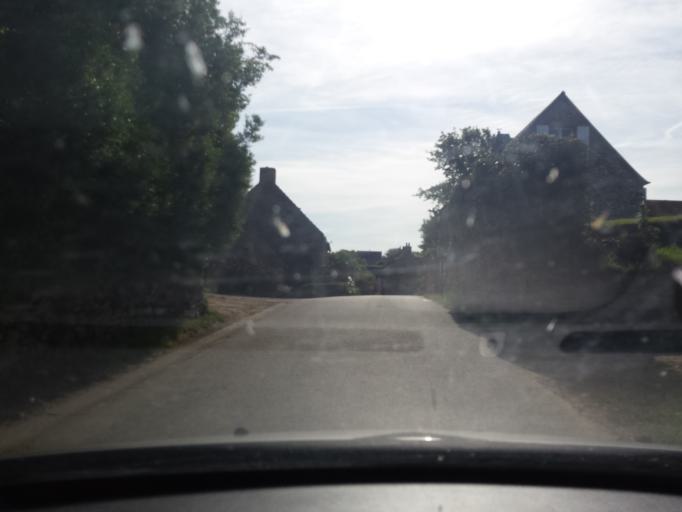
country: FR
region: Lower Normandy
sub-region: Departement de la Manche
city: Beaumont-Hague
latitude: 49.6778
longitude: -1.9200
